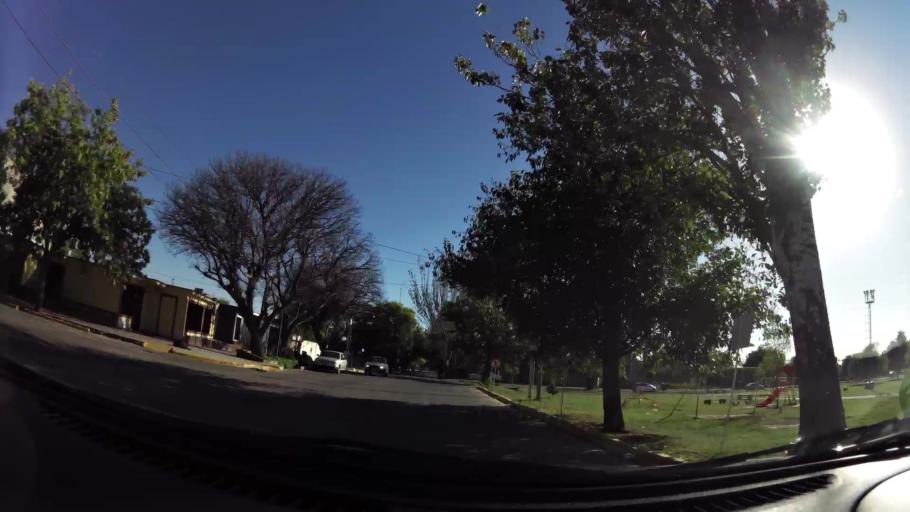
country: AR
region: Mendoza
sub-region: Departamento de Godoy Cruz
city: Godoy Cruz
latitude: -32.9318
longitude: -68.8304
